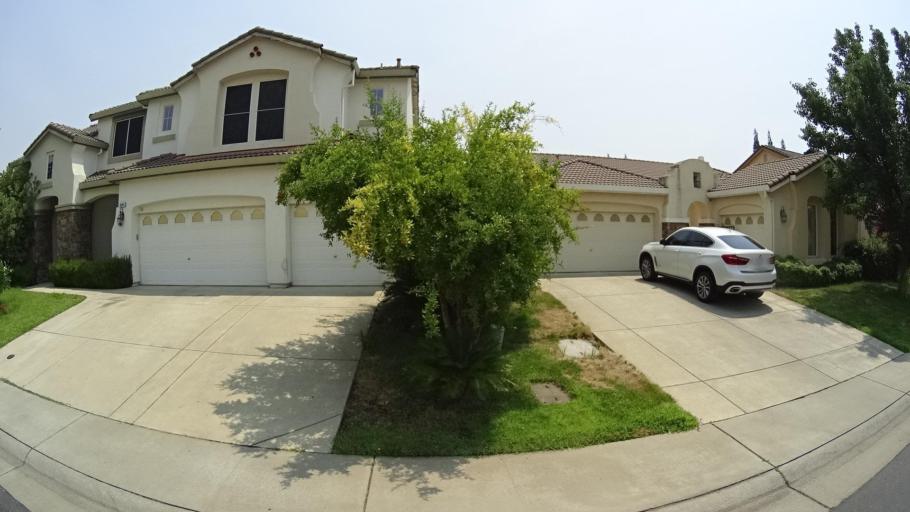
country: US
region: California
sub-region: Placer County
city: Rocklin
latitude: 38.7998
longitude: -121.2777
